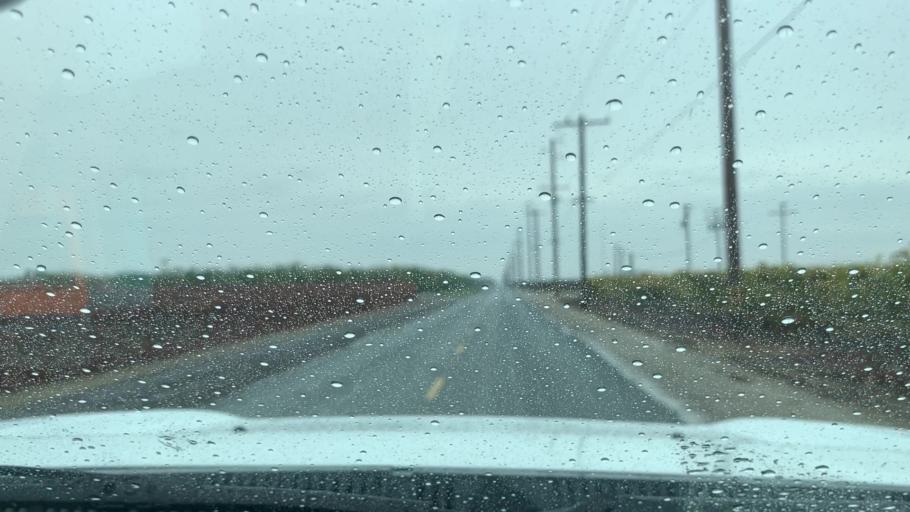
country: US
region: California
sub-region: Tulare County
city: Richgrove
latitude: 35.8342
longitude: -119.1690
